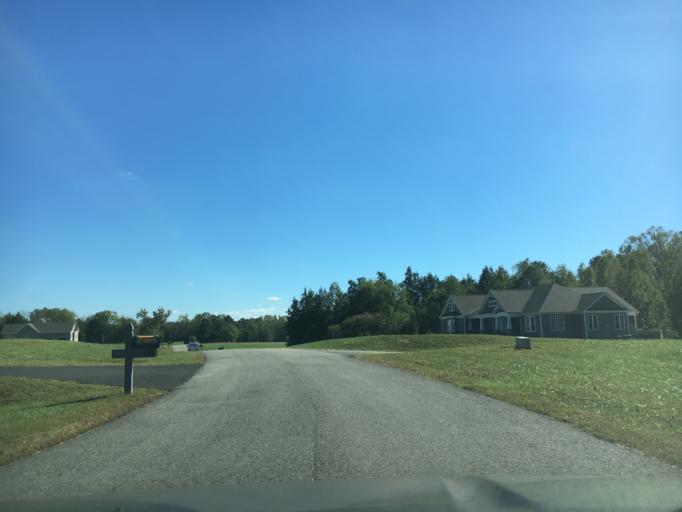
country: US
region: Virginia
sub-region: Goochland County
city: Goochland
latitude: 37.6955
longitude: -77.8379
